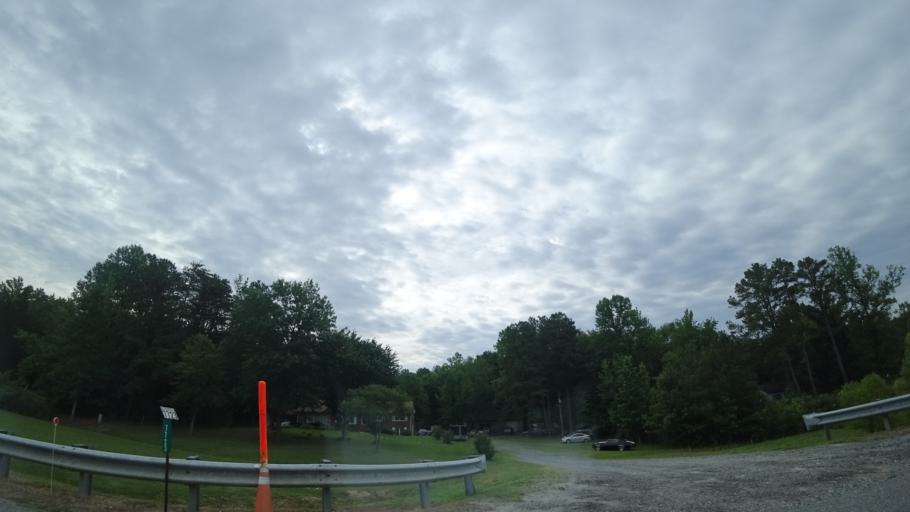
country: US
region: Virginia
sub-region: Spotsylvania County
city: Spotsylvania Courthouse
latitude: 38.1716
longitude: -77.6343
